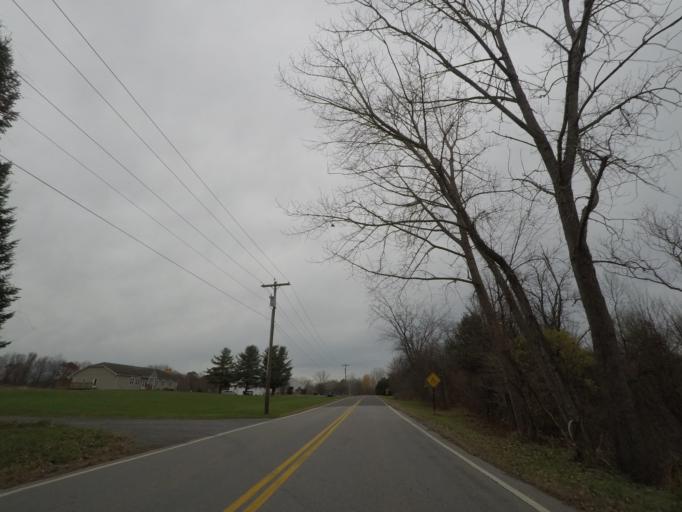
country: US
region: New York
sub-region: Saratoga County
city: Mechanicville
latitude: 42.8498
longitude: -73.6927
